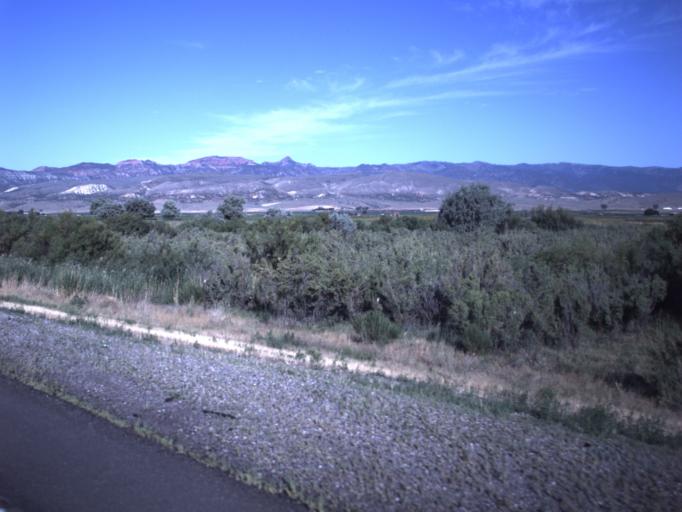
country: US
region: Utah
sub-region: Sevier County
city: Salina
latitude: 38.9386
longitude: -111.8898
